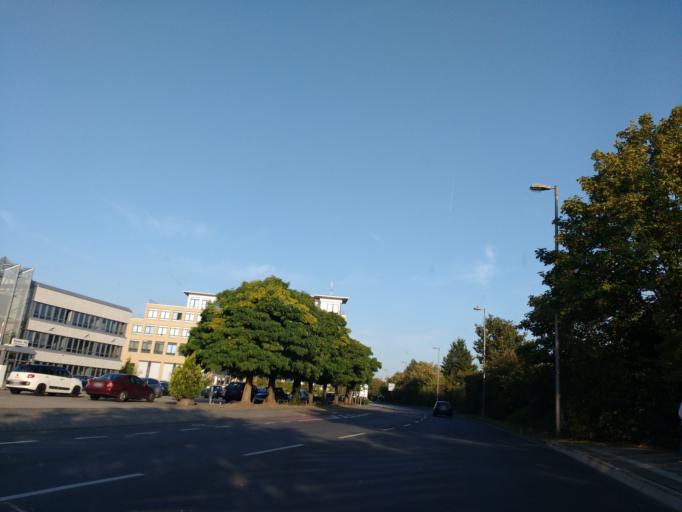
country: DE
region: North Rhine-Westphalia
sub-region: Regierungsbezirk Koln
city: Bilderstoeckchen
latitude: 50.9908
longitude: 6.9059
